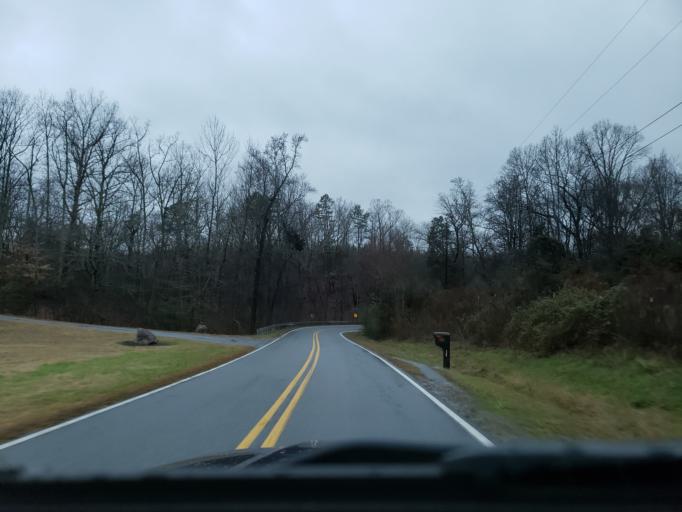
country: US
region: North Carolina
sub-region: Cleveland County
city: White Plains
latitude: 35.1881
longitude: -81.3820
